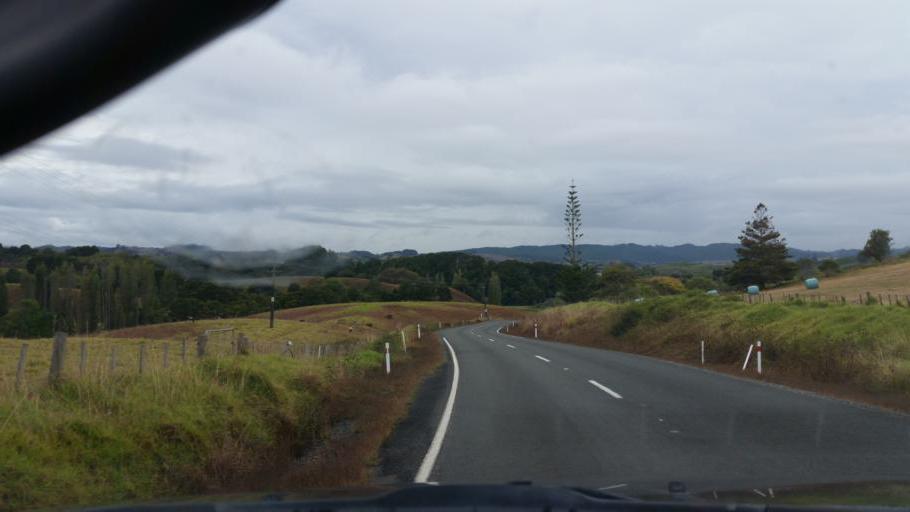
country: NZ
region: Auckland
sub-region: Auckland
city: Wellsford
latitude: -36.1260
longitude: 174.3585
